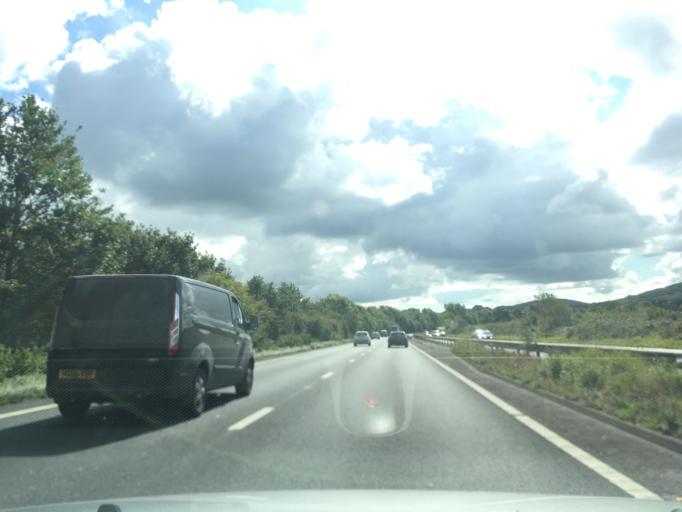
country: GB
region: England
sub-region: Hampshire
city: Petersfield
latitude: 51.0033
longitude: -0.9523
